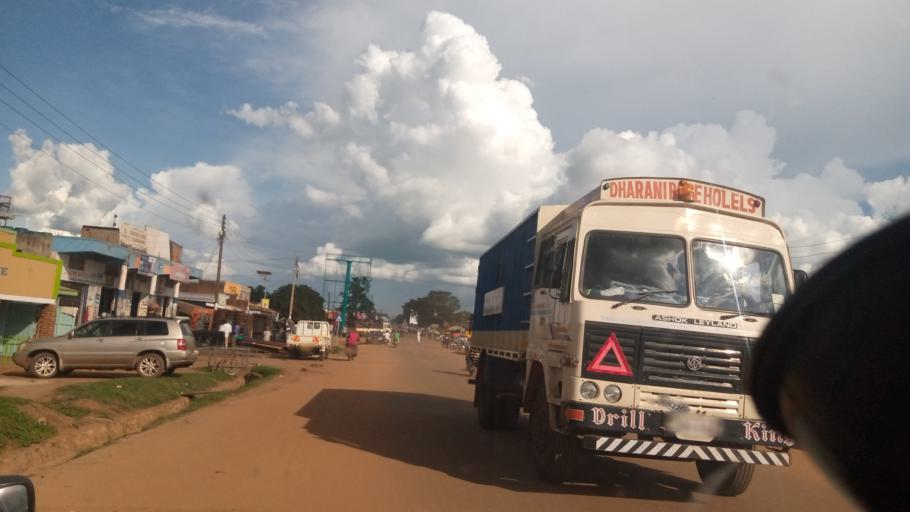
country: UG
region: Northern Region
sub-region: Lira District
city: Lira
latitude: 2.2417
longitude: 32.8881
